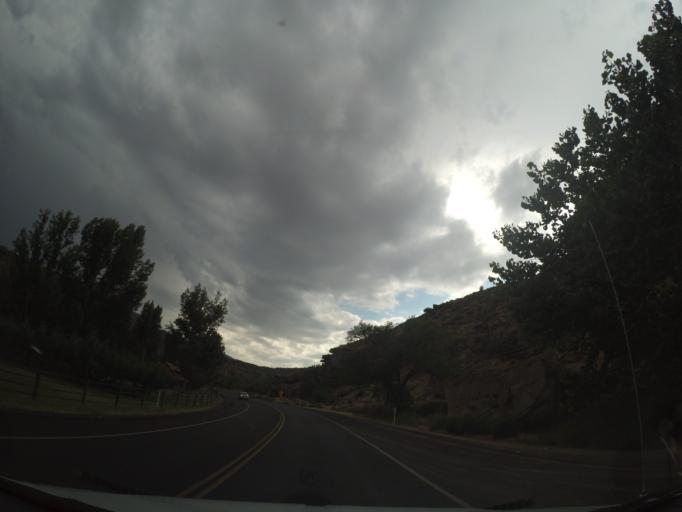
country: US
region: Utah
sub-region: Washington County
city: Hildale
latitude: 37.1630
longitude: -113.0173
